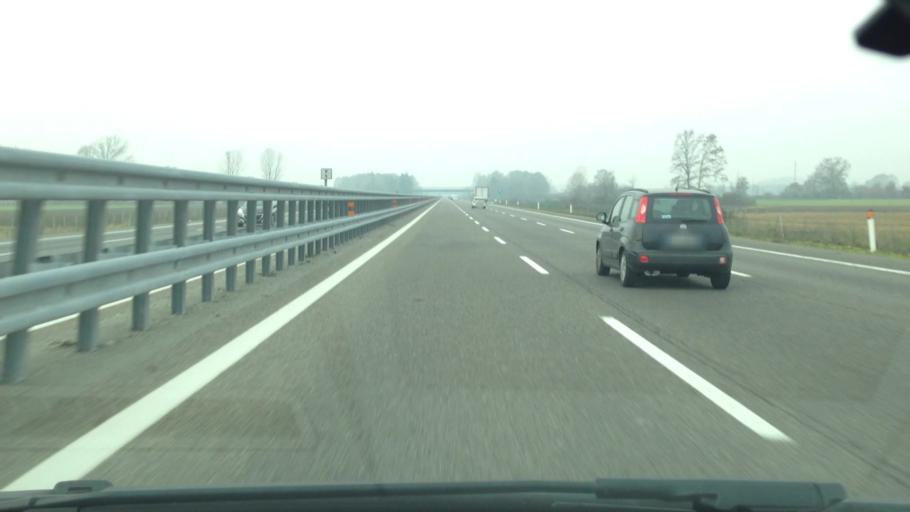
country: IT
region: Piedmont
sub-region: Provincia di Torino
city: Pessione
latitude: 44.9528
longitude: 7.8569
